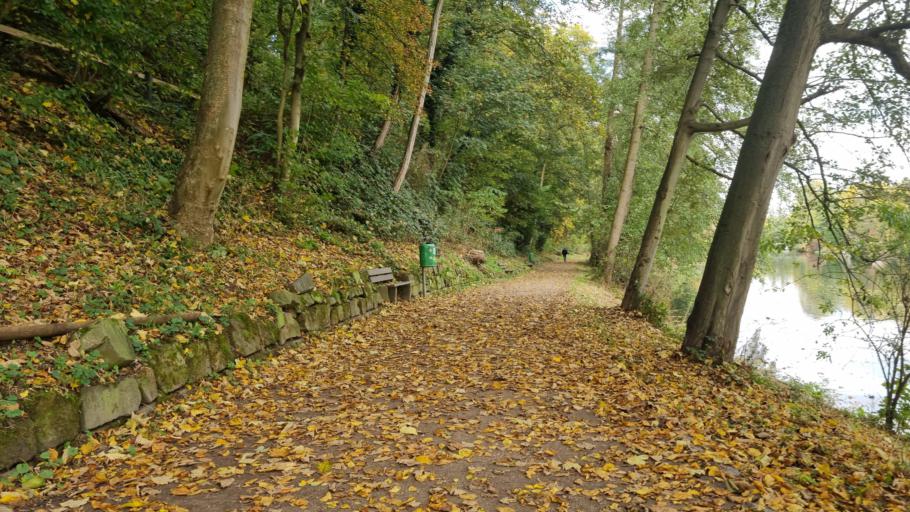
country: DE
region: North Rhine-Westphalia
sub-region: Regierungsbezirk Dusseldorf
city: Kleve
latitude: 51.7823
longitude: 6.1392
